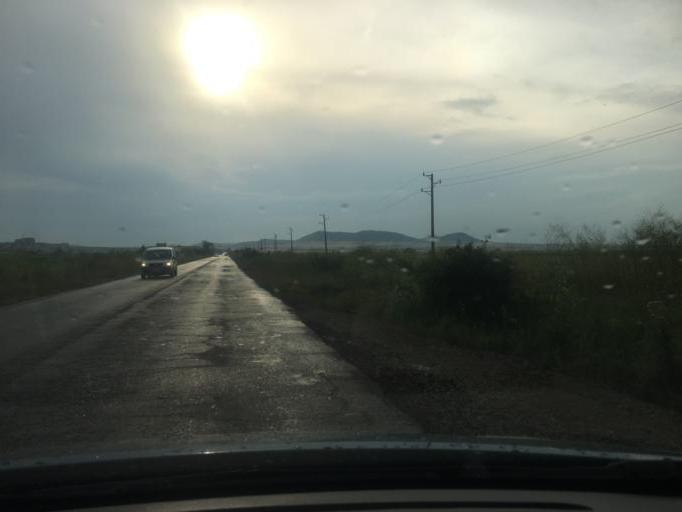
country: BG
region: Burgas
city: Aheloy
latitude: 42.6461
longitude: 27.6348
